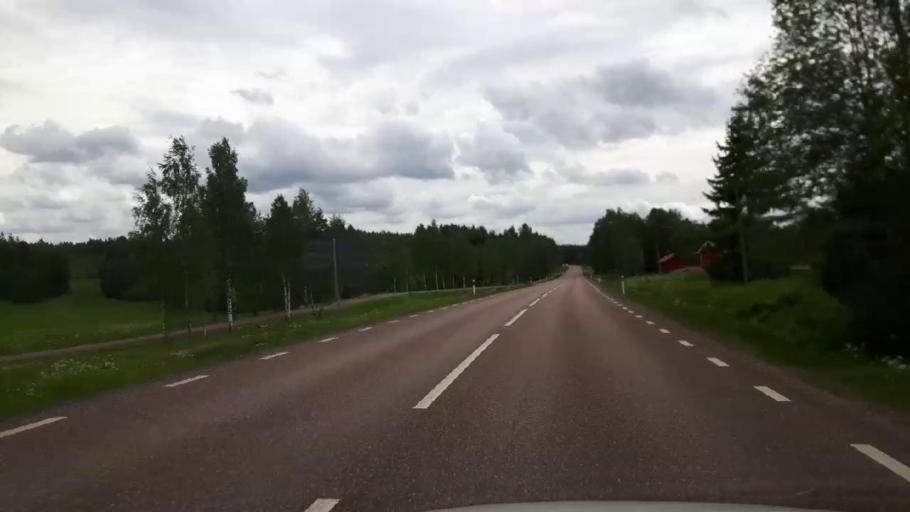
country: SE
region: Dalarna
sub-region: Hedemora Kommun
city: Brunna
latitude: 60.2142
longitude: 15.9919
